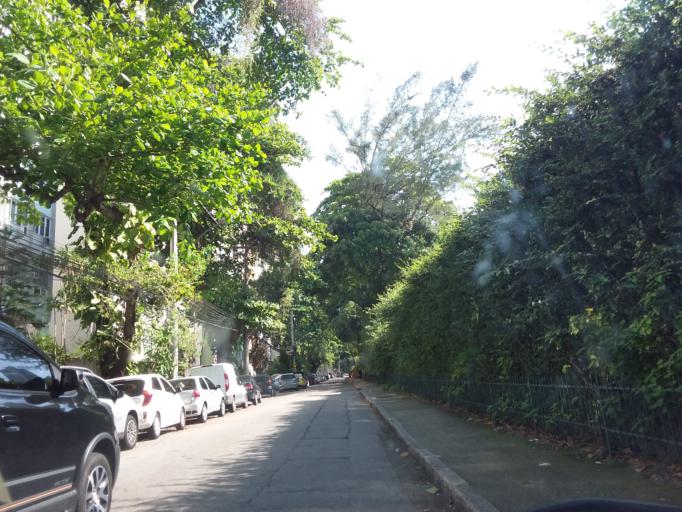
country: BR
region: Rio de Janeiro
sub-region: Rio De Janeiro
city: Rio de Janeiro
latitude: -22.9550
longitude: -43.1751
